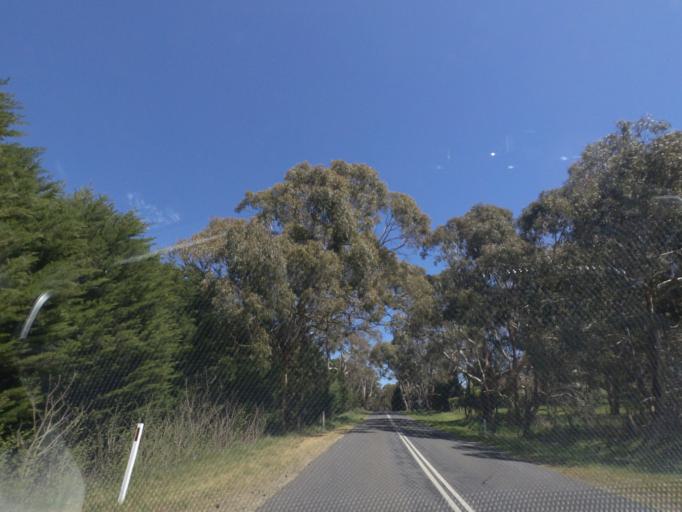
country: AU
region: Victoria
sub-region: Hume
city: Sunbury
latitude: -37.3139
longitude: 144.6740
